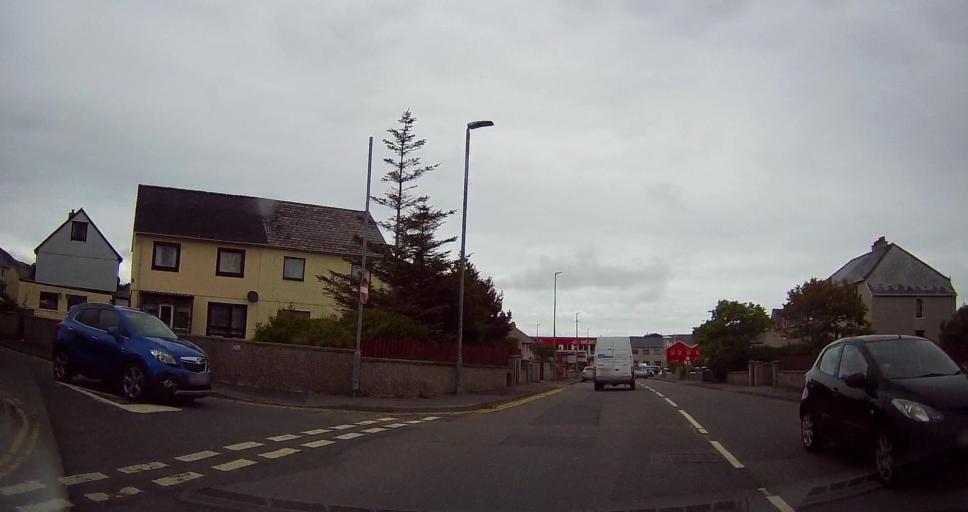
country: GB
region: Scotland
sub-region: Shetland Islands
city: Lerwick
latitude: 60.1568
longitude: -1.1591
